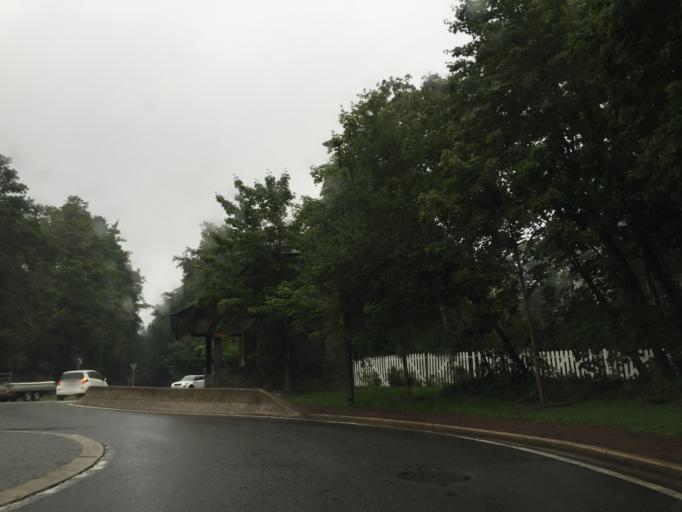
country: BE
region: Wallonia
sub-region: Province de Liege
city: Spa
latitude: 50.5030
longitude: 5.8845
